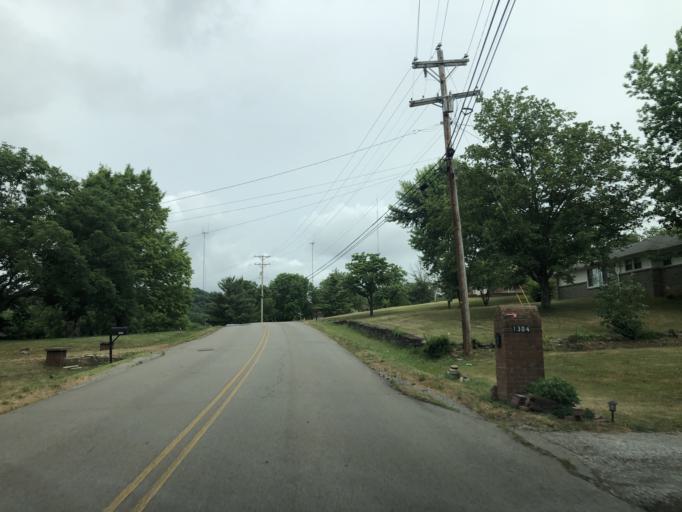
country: US
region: Tennessee
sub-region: Davidson County
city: Goodlettsville
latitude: 36.2621
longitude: -86.7702
